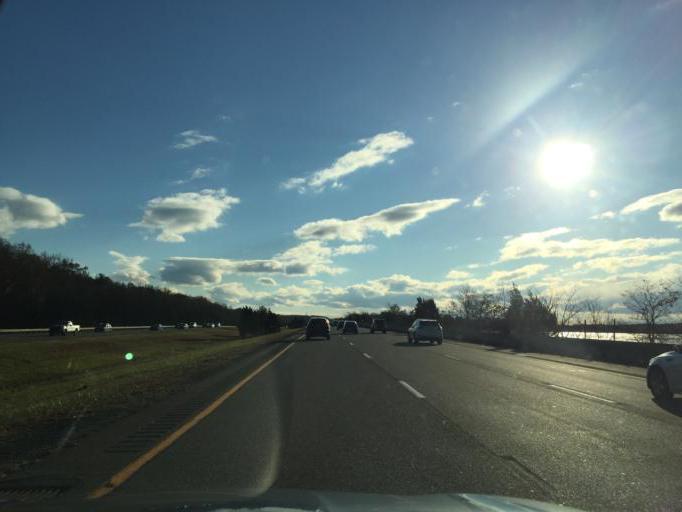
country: US
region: Massachusetts
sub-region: Bristol County
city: Attleboro
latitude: 41.9474
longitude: -71.3097
